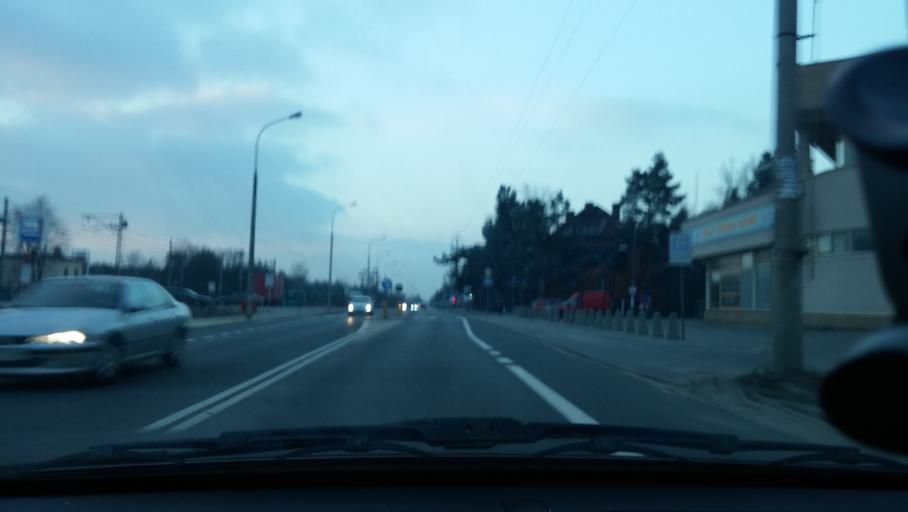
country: PL
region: Masovian Voivodeship
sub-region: Warszawa
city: Wawer
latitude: 52.1916
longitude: 21.1818
